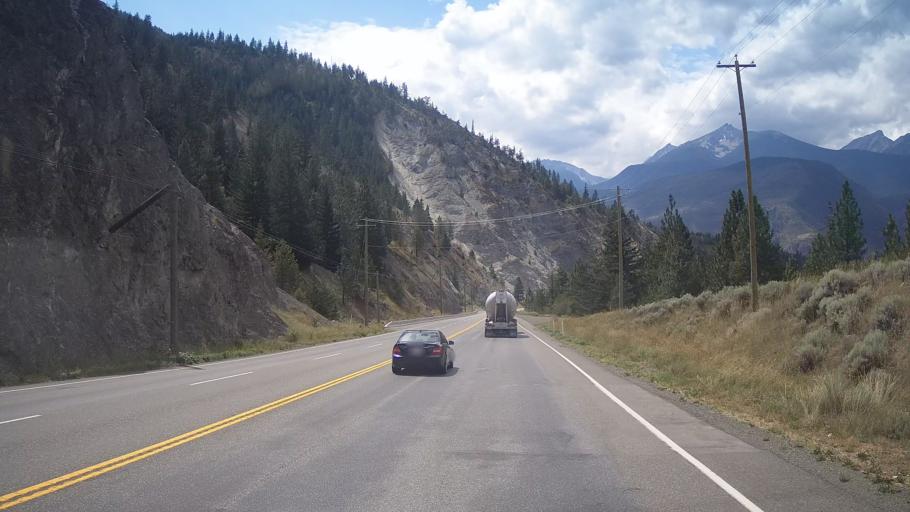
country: CA
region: British Columbia
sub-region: Thompson-Nicola Regional District
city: Ashcroft
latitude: 50.2537
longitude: -121.5454
